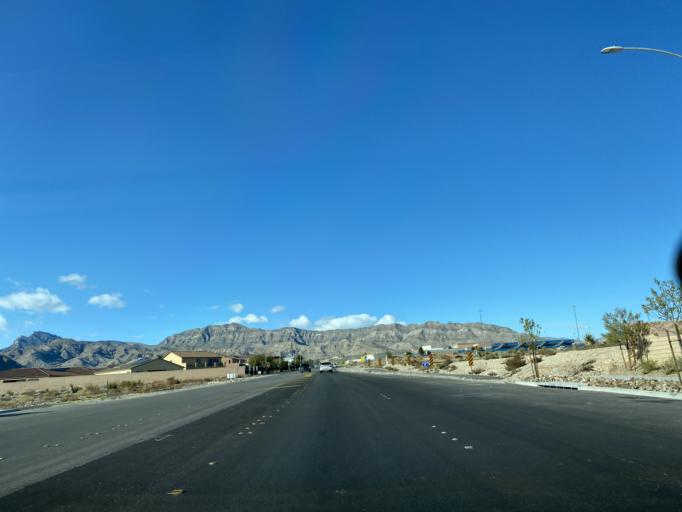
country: US
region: Nevada
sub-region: Clark County
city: Summerlin South
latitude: 36.2774
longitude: -115.3113
